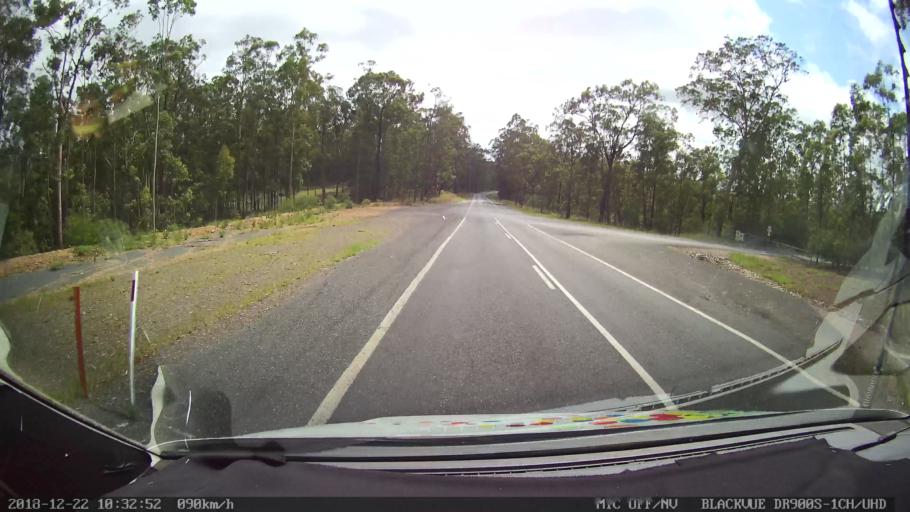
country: AU
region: New South Wales
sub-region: Clarence Valley
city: South Grafton
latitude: -29.6181
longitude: 152.6462
